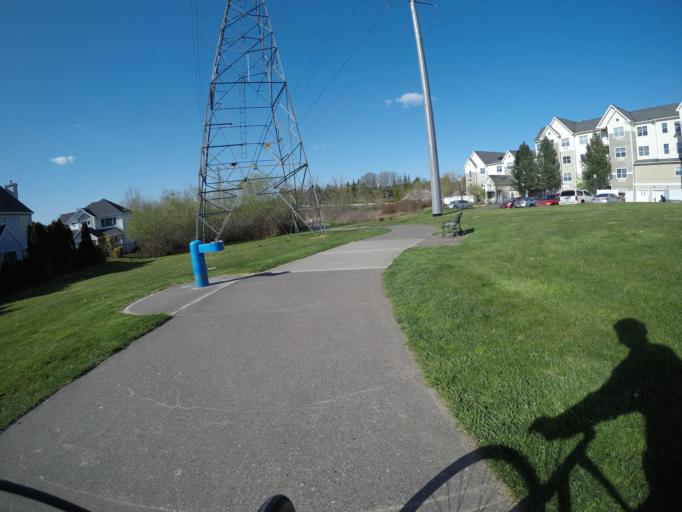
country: US
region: Oregon
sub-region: Washington County
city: Oak Hills
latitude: 45.5492
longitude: -122.8473
